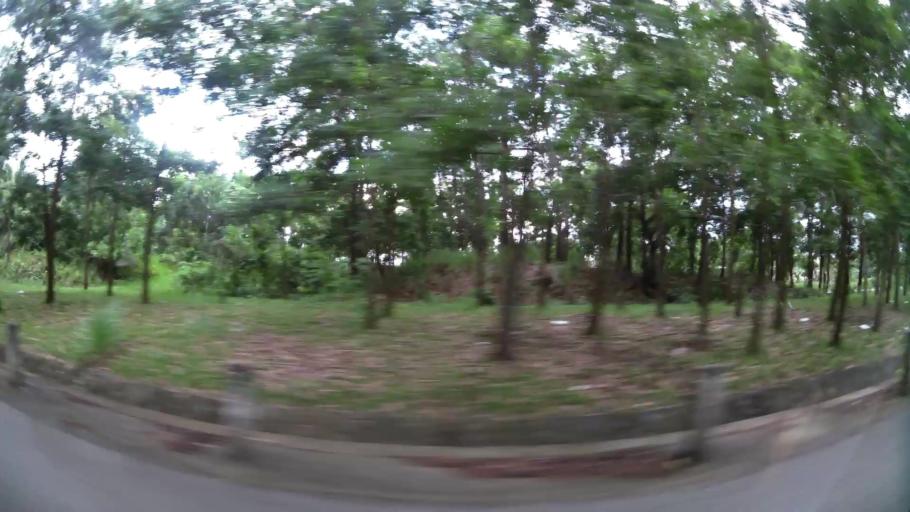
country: DO
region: San Cristobal
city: Villa Altagracia
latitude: 18.6465
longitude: -70.1693
